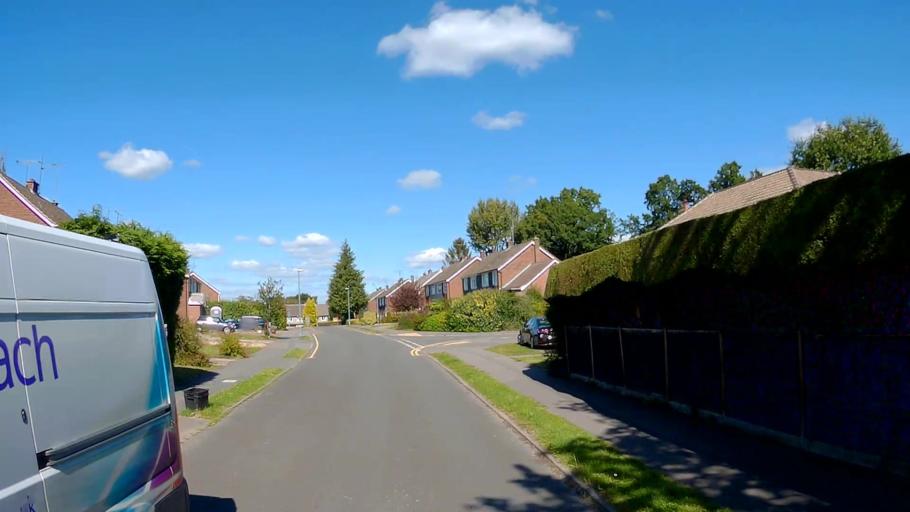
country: GB
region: England
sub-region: Bracknell Forest
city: Crowthorne
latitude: 51.3758
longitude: -0.8002
